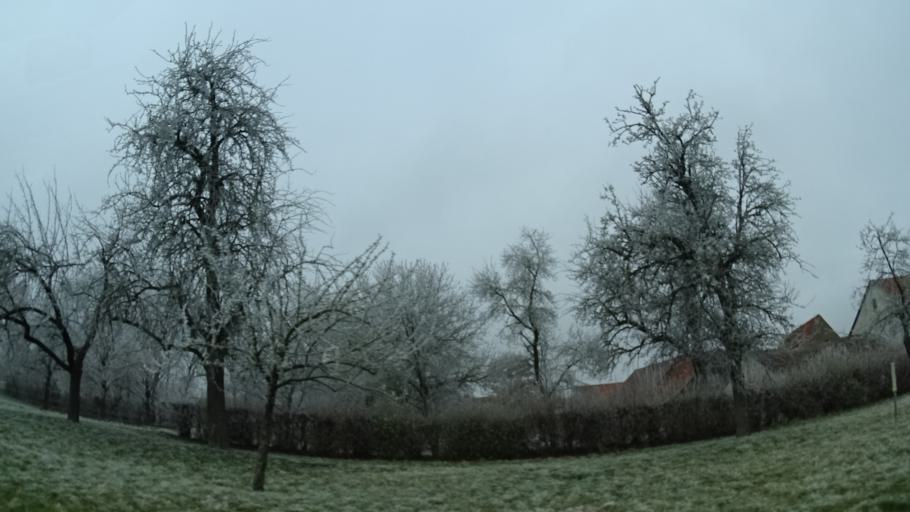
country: DE
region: Bavaria
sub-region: Regierungsbezirk Unterfranken
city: Butthard
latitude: 49.6056
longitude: 9.9065
